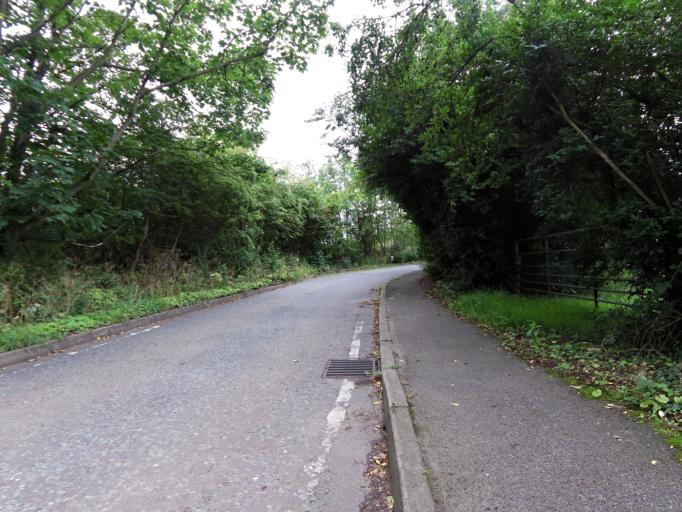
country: GB
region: England
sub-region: Hertfordshire
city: Hatfield
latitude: 51.7386
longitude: -0.2656
